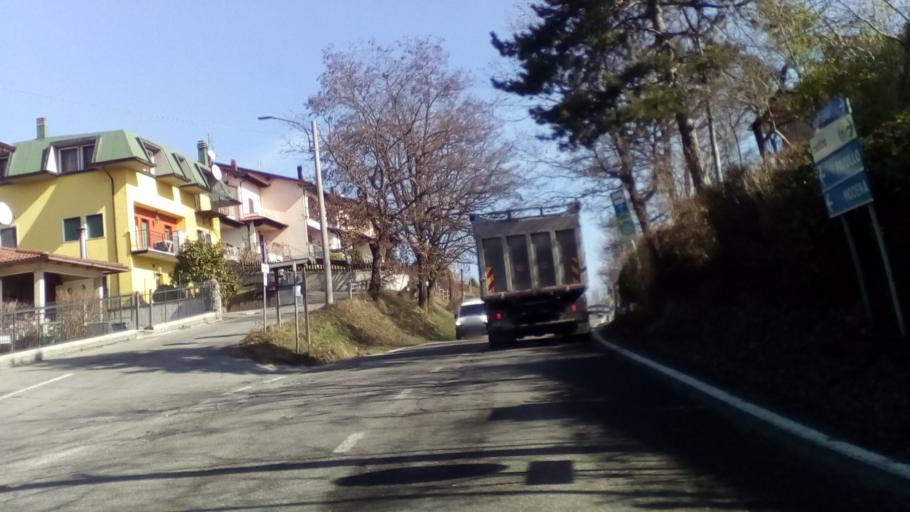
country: IT
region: Emilia-Romagna
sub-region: Provincia di Modena
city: Lama
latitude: 44.3087
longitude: 10.7393
